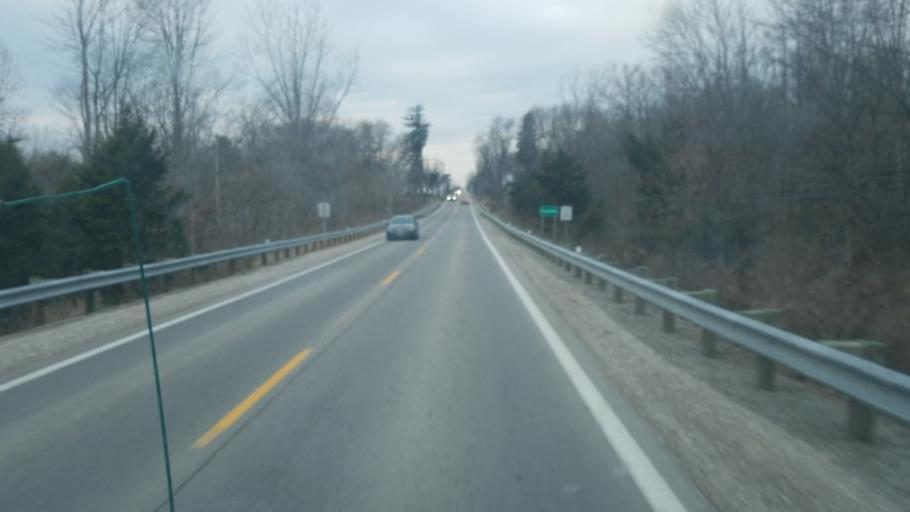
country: US
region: Ohio
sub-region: Delaware County
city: Ashley
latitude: 40.3299
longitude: -82.9542
